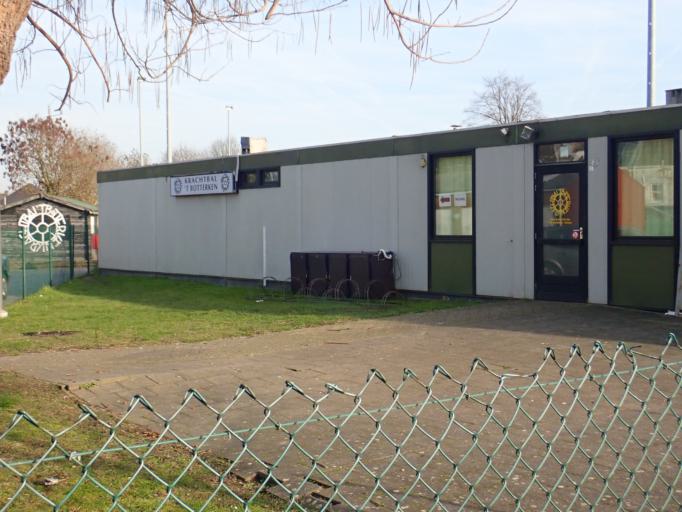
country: BE
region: Flanders
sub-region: Provincie Oost-Vlaanderen
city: Lebbeke
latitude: 51.0350
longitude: 4.1635
